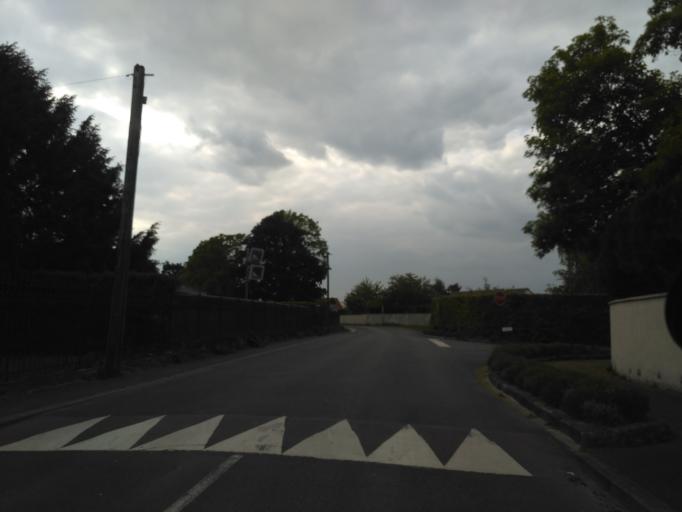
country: FR
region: Ile-de-France
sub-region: Departement de Seine-et-Marne
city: Voisenon
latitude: 48.5717
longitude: 2.6600
